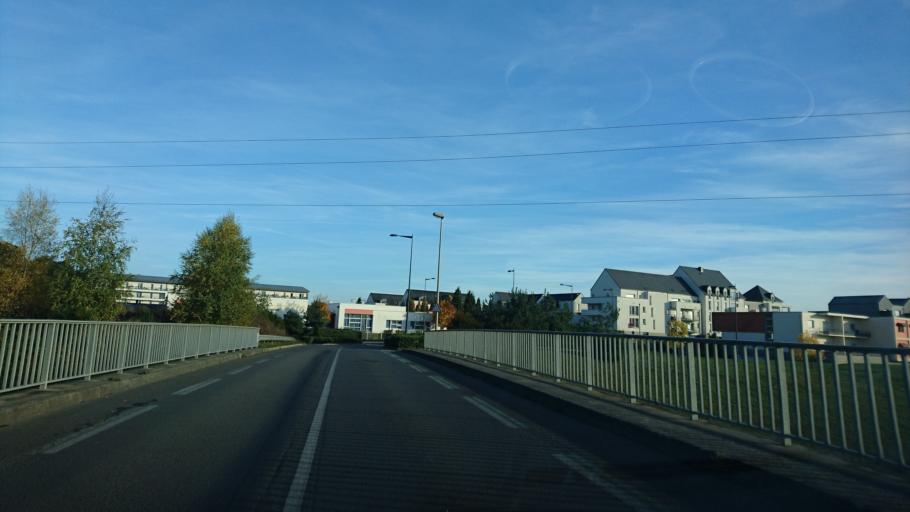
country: FR
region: Brittany
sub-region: Departement d'Ille-et-Vilaine
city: Bruz
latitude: 48.0312
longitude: -1.7608
